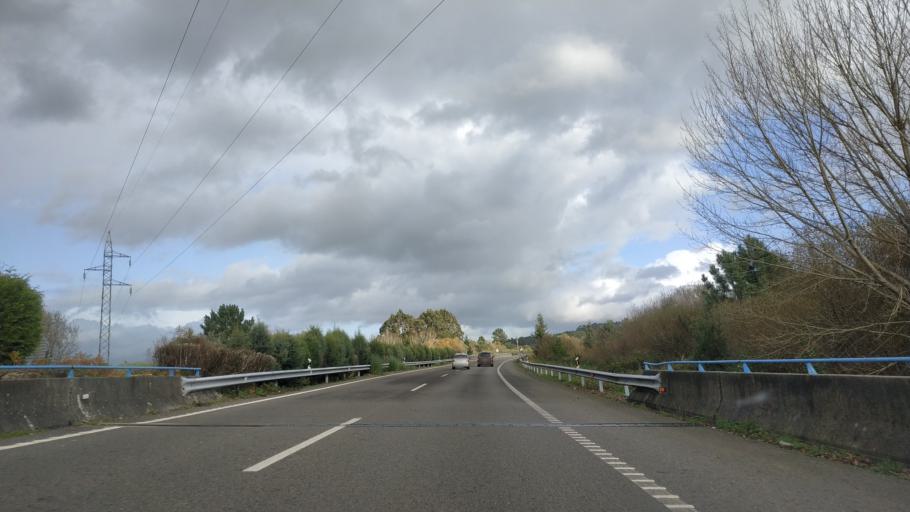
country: ES
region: Galicia
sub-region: Provincia da Coruna
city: Betanzos
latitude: 43.2607
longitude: -8.2562
